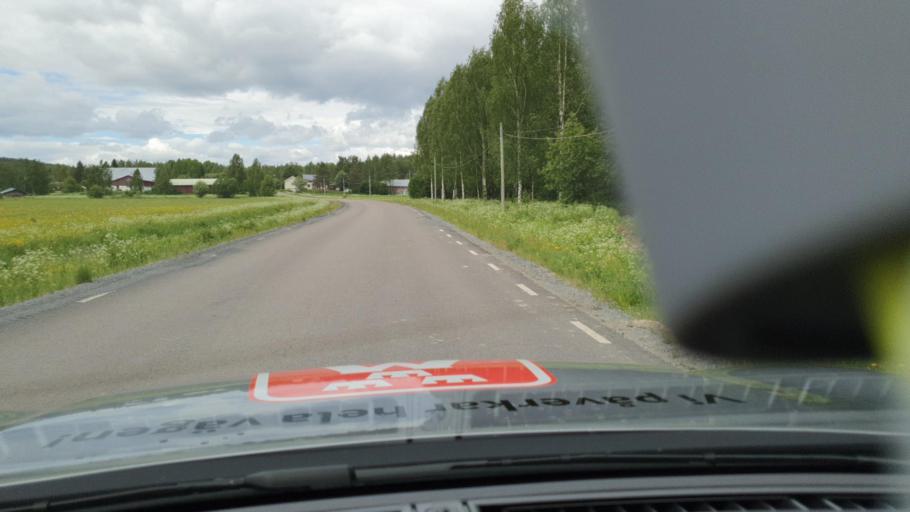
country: SE
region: Norrbotten
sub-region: Lulea Kommun
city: Sodra Sunderbyn
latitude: 65.8452
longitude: 21.9241
